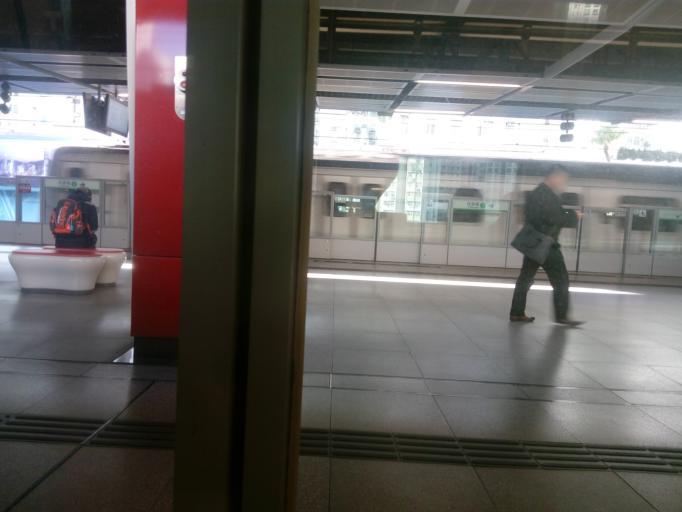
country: HK
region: Kowloon City
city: Kowloon
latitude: 22.3231
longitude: 114.2142
